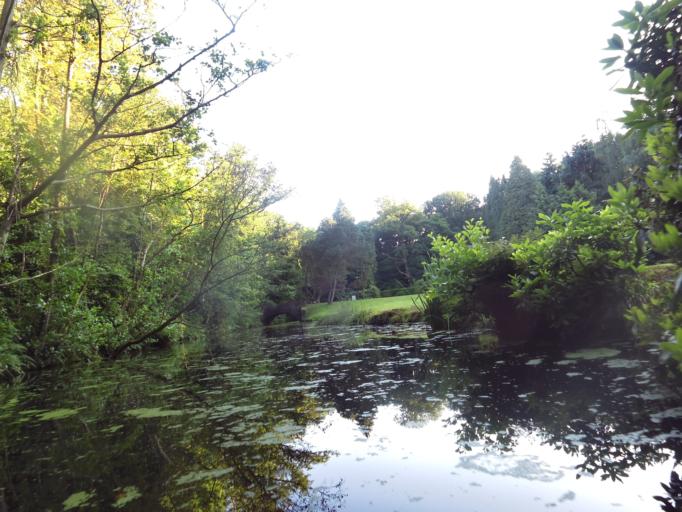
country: NL
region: South Holland
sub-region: Gemeente Wassenaar
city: Wassenaar
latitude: 52.1343
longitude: 4.3849
